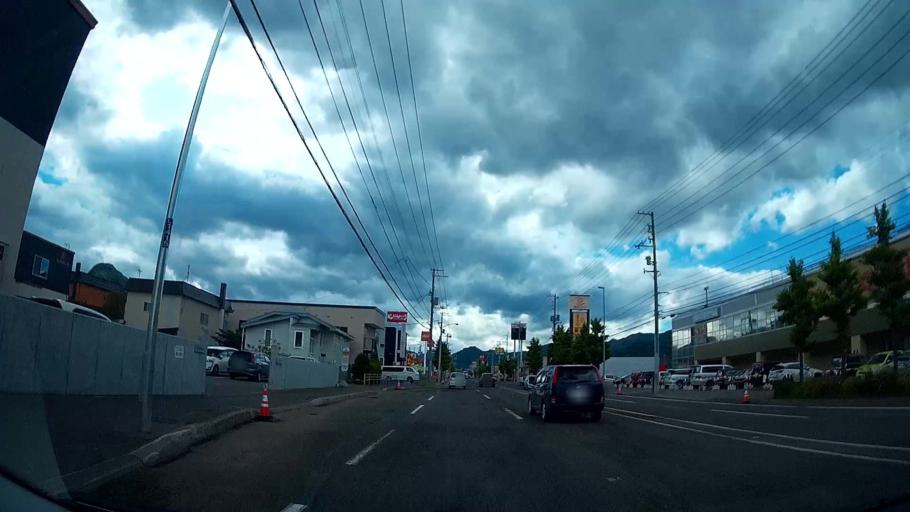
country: JP
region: Hokkaido
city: Sapporo
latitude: 42.9613
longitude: 141.3030
